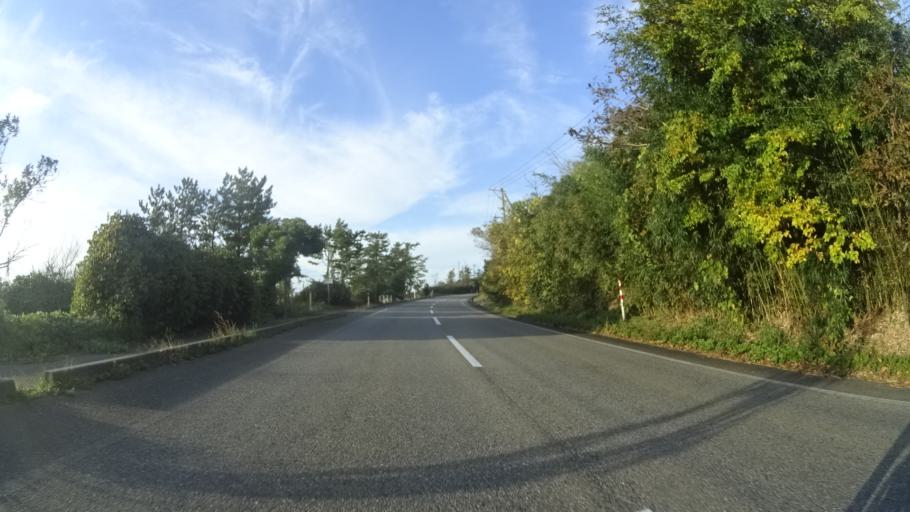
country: JP
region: Ishikawa
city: Hakui
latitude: 37.1062
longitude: 136.7290
